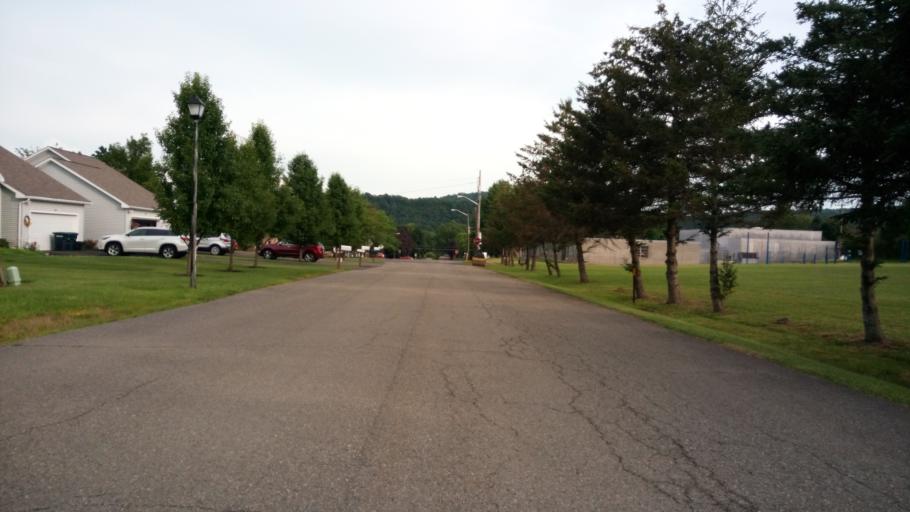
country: US
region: New York
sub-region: Chemung County
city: West Elmira
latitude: 42.0840
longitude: -76.8376
